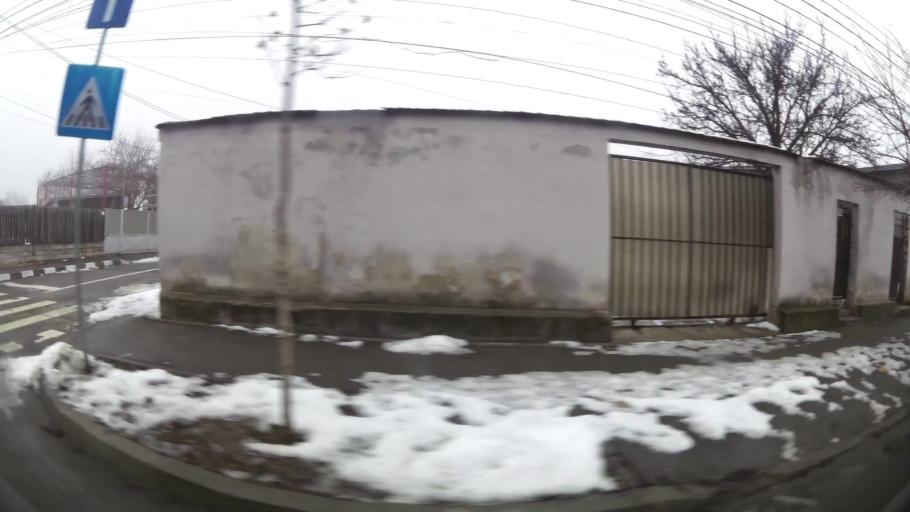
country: RO
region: Ilfov
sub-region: Comuna Chiajna
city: Rosu
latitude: 44.4684
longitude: 26.0097
